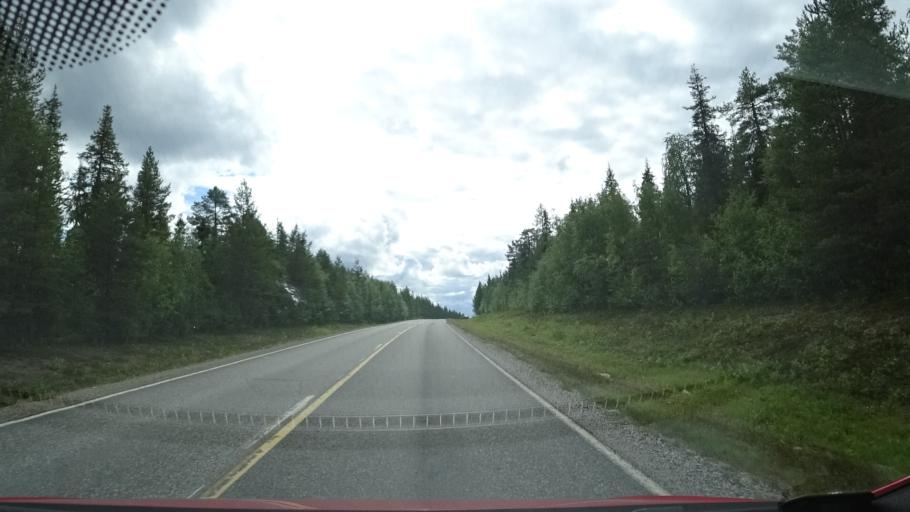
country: FI
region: Lapland
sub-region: Tunturi-Lappi
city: Kittilae
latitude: 67.5571
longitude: 24.9225
